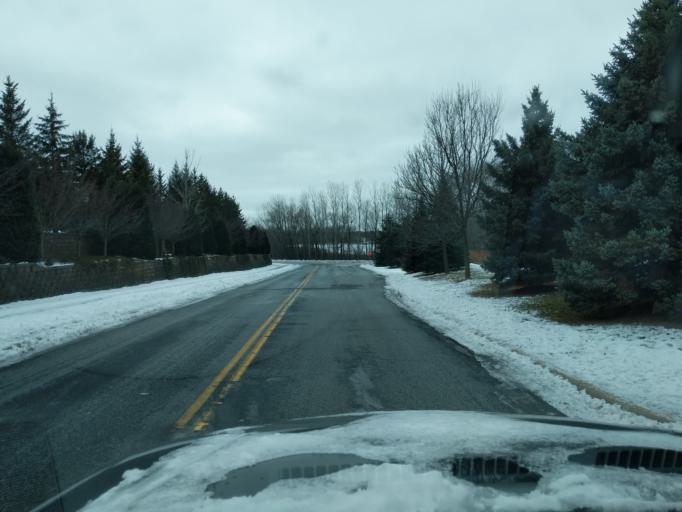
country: US
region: Minnesota
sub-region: Hennepin County
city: Eden Prairie
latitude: 44.8516
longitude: -93.4354
